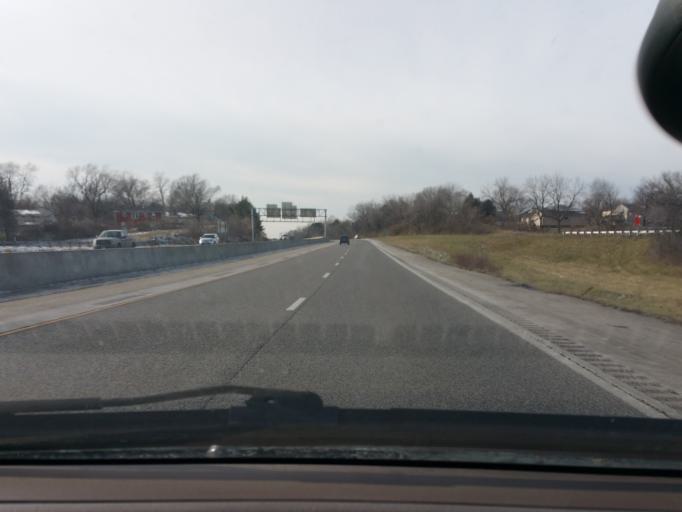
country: US
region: Missouri
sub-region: Clay County
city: Claycomo
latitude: 39.2058
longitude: -94.4944
